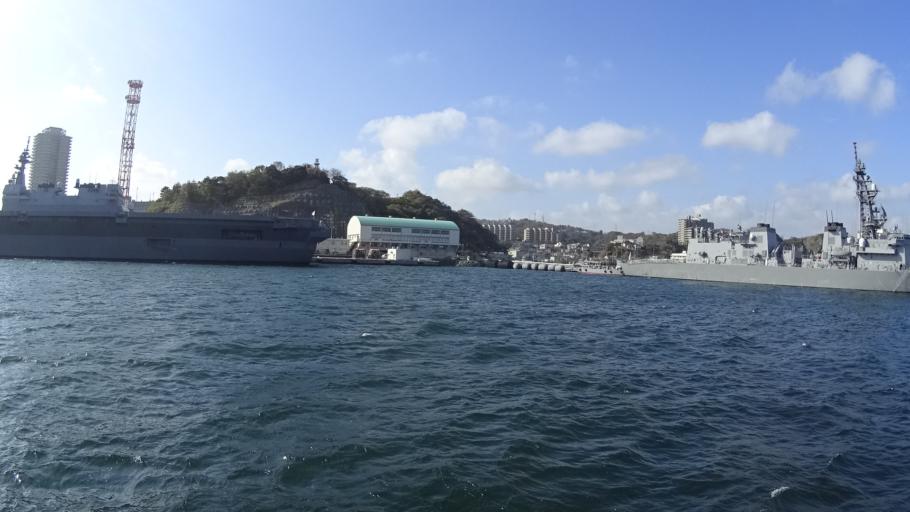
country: JP
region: Kanagawa
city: Yokosuka
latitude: 35.2891
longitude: 139.6546
